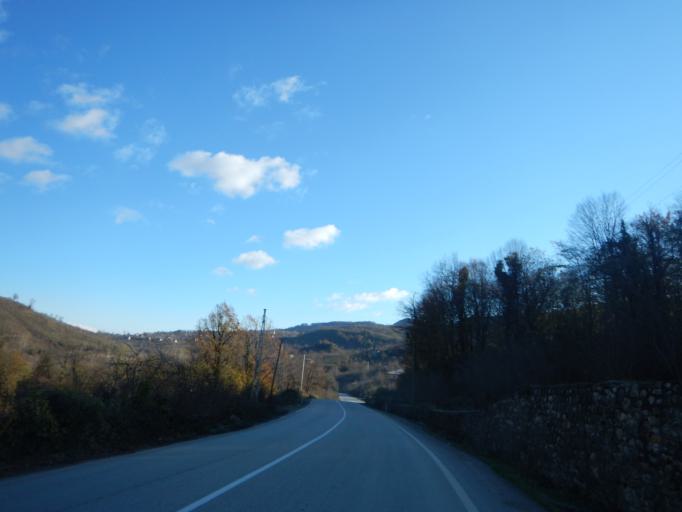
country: TR
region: Ordu
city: Kumru
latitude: 40.8887
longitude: 37.3054
